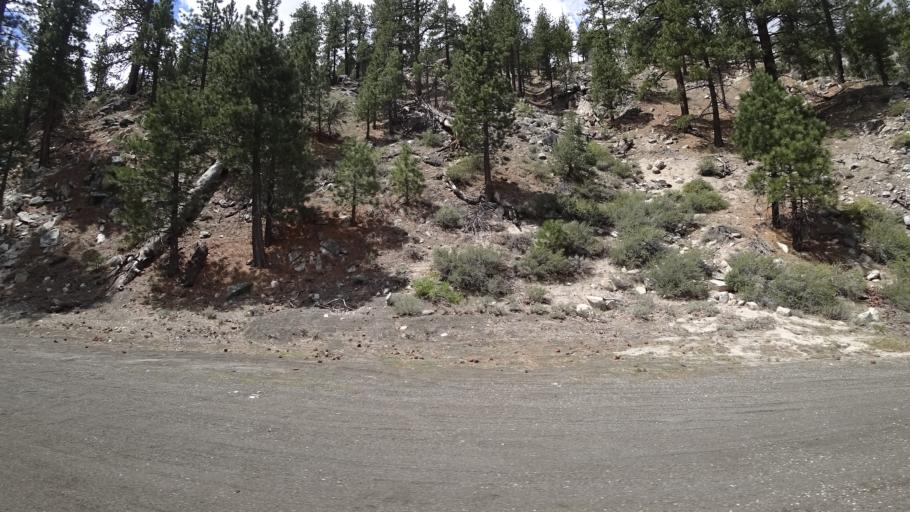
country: US
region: California
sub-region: Mono County
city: Bridgeport
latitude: 38.4543
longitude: -119.4603
